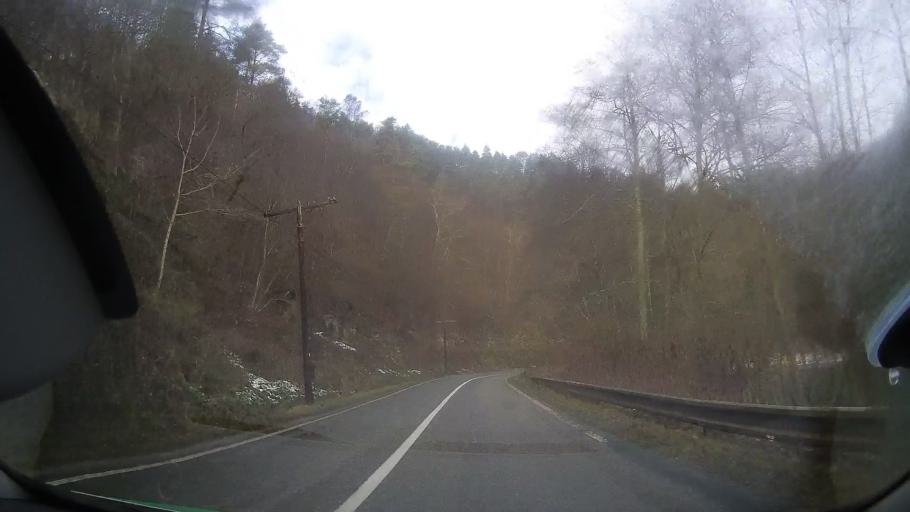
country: RO
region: Alba
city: Salciua de Sus
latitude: 46.4163
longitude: 23.4575
